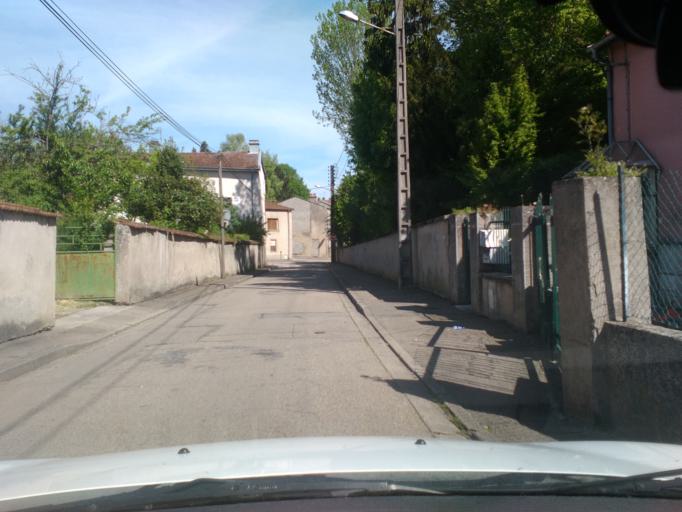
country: FR
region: Lorraine
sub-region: Departement des Vosges
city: Mirecourt
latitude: 48.2982
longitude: 6.1355
